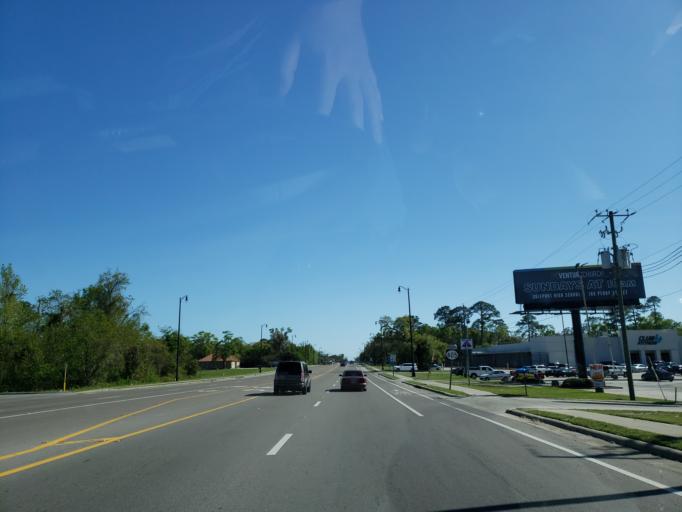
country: US
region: Mississippi
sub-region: Harrison County
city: West Gulfport
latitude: 30.3982
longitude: -89.0269
